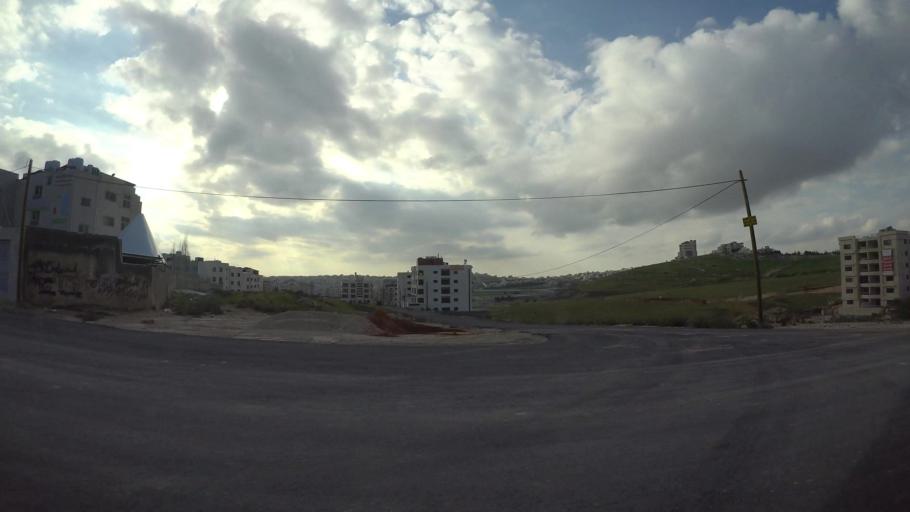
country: JO
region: Amman
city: Al Bunayyat ash Shamaliyah
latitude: 31.9085
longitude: 35.8702
